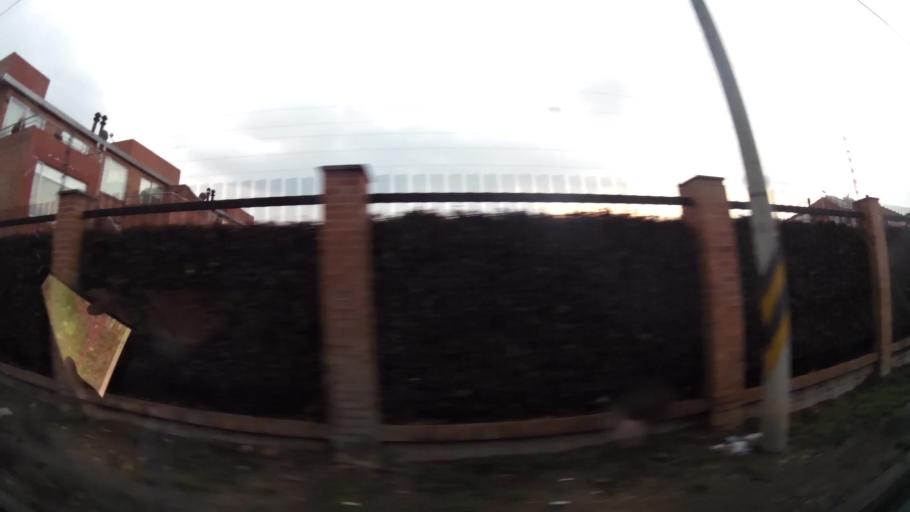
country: CO
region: Cundinamarca
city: Chia
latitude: 4.8507
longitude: -74.0623
